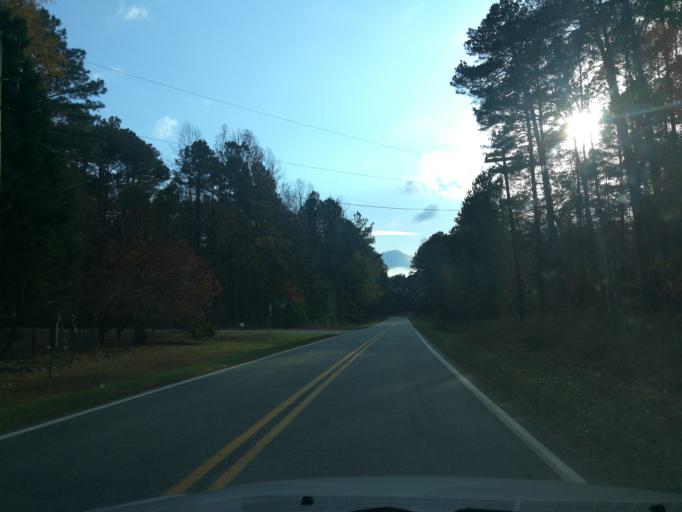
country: US
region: North Carolina
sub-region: Durham County
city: Durham
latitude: 36.0019
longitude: -78.9926
